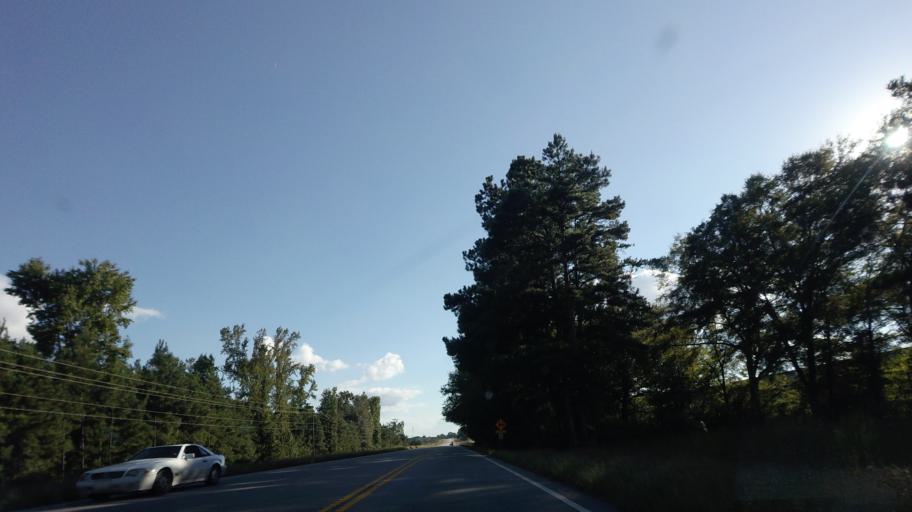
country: US
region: Georgia
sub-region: Upson County
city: Thomaston
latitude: 32.9547
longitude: -84.2512
